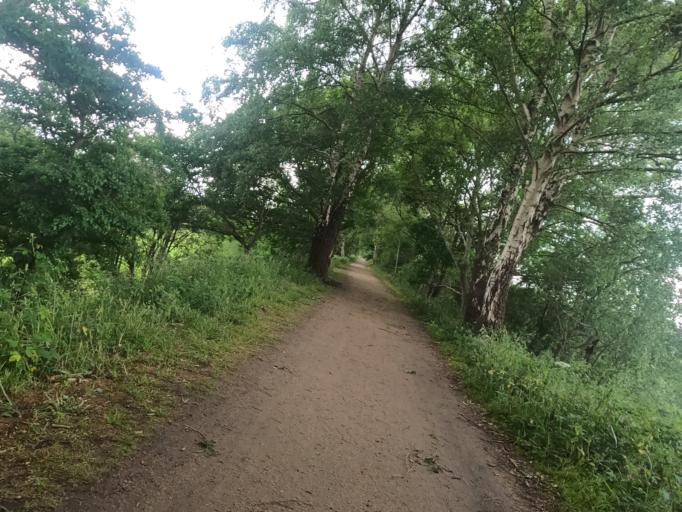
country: GB
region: England
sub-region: Cheshire West and Chester
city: Over
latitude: 53.2051
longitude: -2.5444
